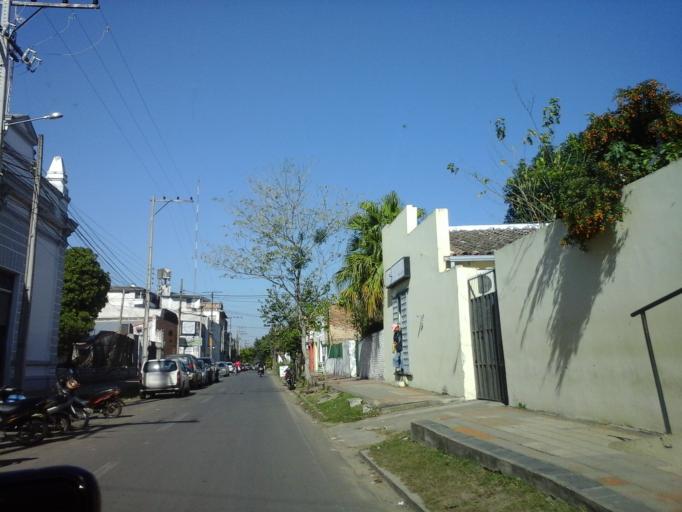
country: PY
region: Neembucu
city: Pilar
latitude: -26.8558
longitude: -58.3075
